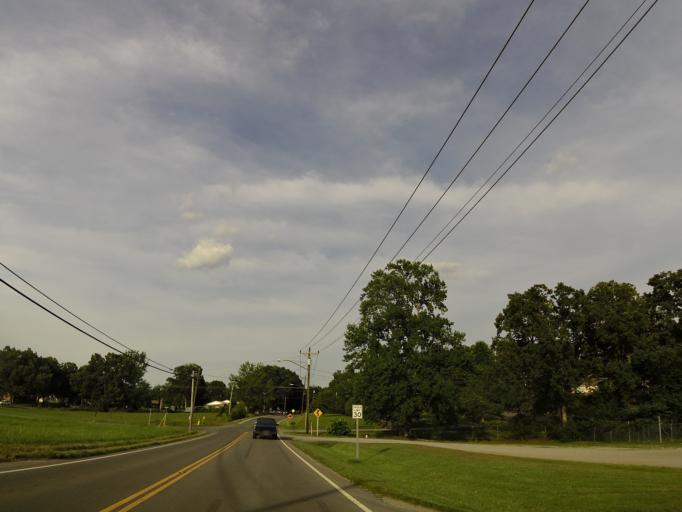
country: US
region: Tennessee
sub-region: Dickson County
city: Dickson
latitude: 36.0654
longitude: -87.3641
